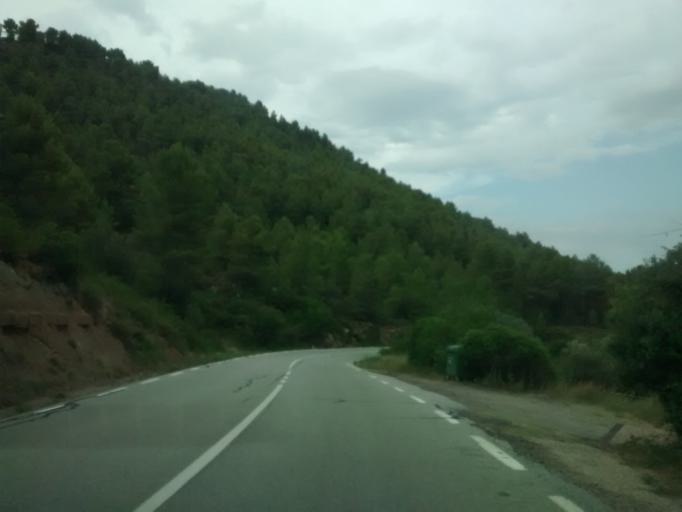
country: ES
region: Catalonia
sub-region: Provincia de Barcelona
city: Fonollosa
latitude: 41.7619
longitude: 1.6989
